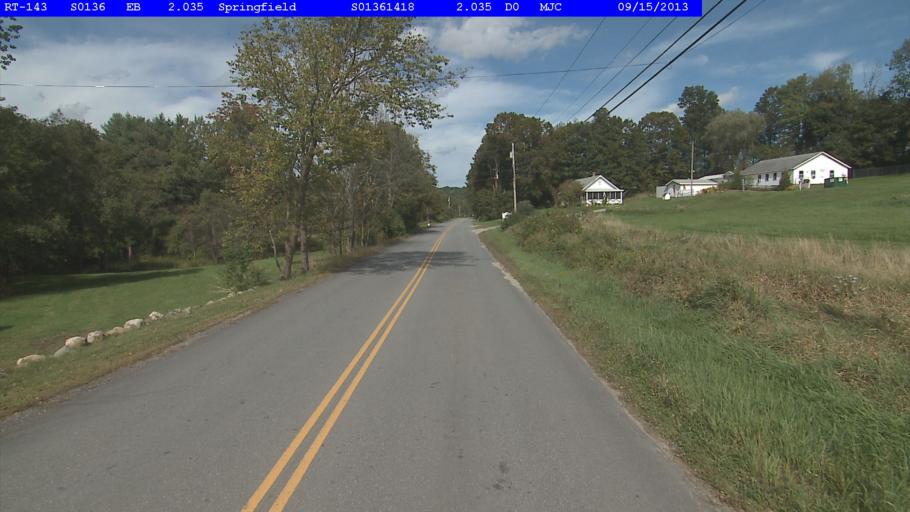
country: US
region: Vermont
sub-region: Windsor County
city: Springfield
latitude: 43.2938
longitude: -72.4495
